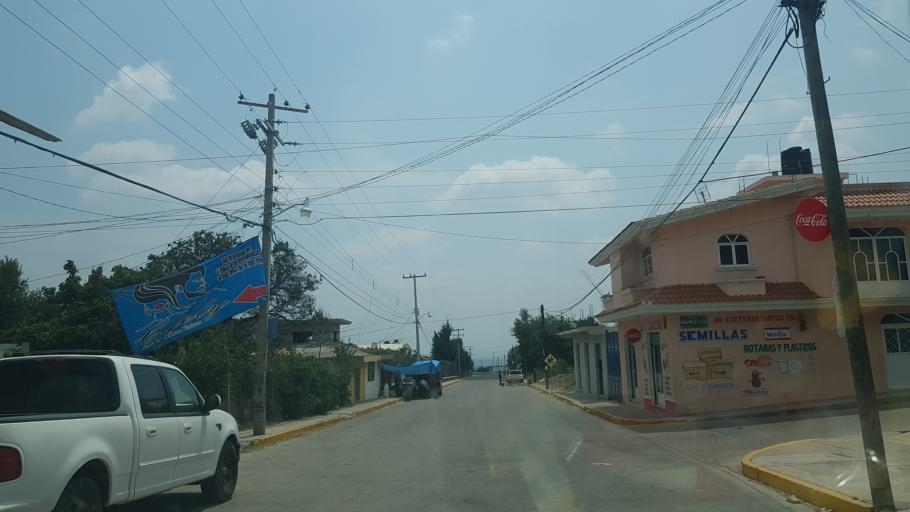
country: MX
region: Puebla
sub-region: Huejotzingo
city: San Juan Pancoac
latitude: 19.1391
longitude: -98.4458
